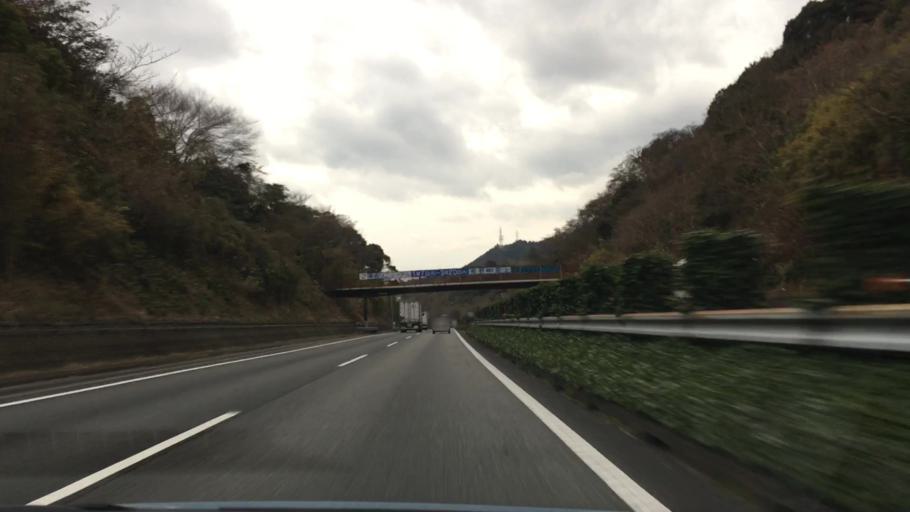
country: JP
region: Shizuoka
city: Fujinomiya
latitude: 35.1511
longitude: 138.6162
